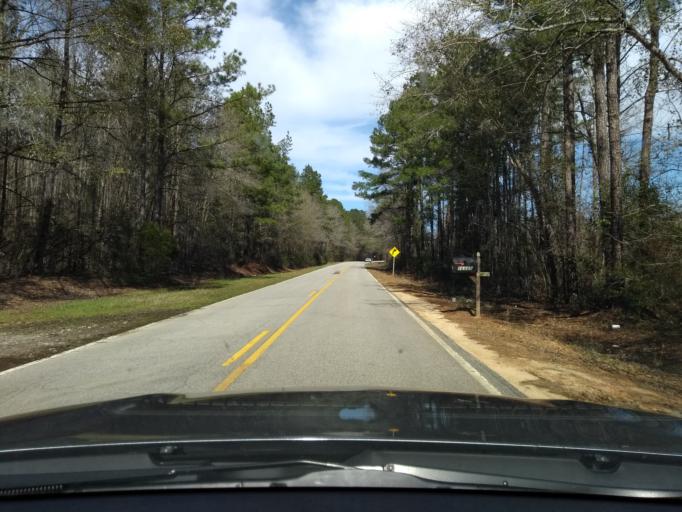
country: US
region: Georgia
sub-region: Bulloch County
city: Brooklet
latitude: 32.4799
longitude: -81.6308
